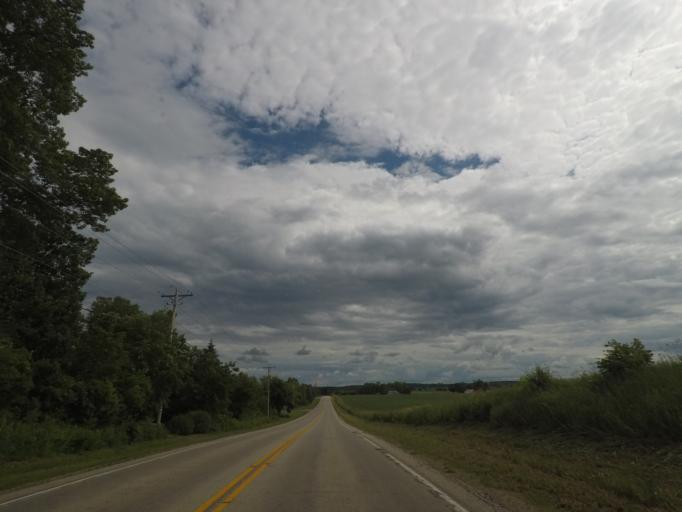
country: US
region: Wisconsin
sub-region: Dane County
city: Belleville
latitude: 42.8337
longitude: -89.5256
